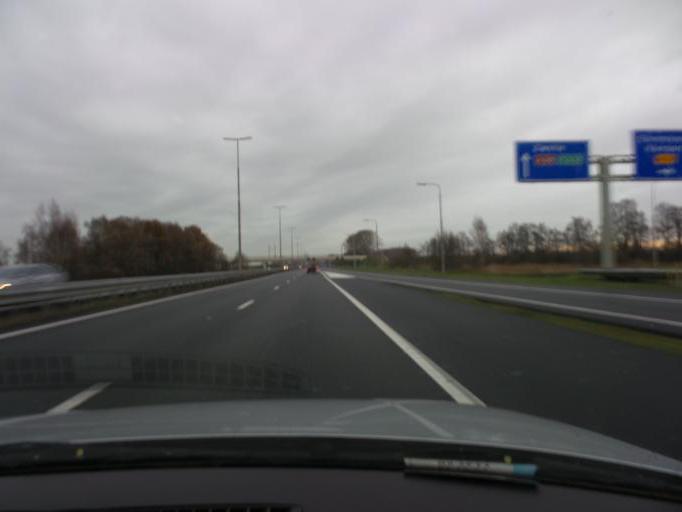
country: NL
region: Gelderland
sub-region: Gemeente Hattem
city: Hattem
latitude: 52.4871
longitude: 6.0253
